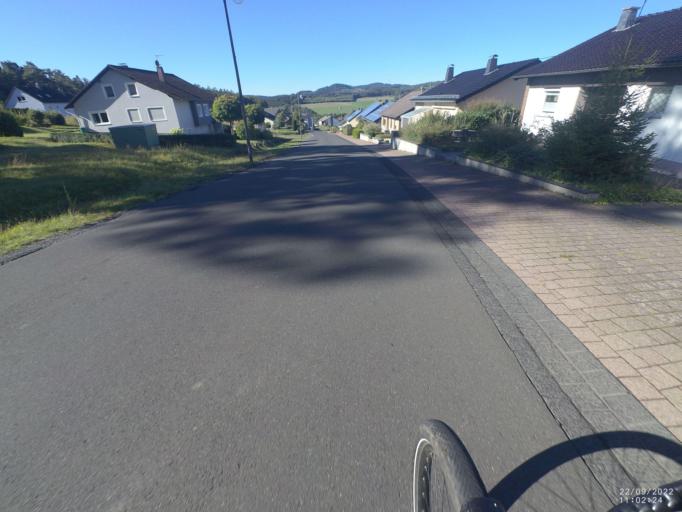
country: DE
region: Rheinland-Pfalz
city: Dockweiler
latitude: 50.2300
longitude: 6.8022
